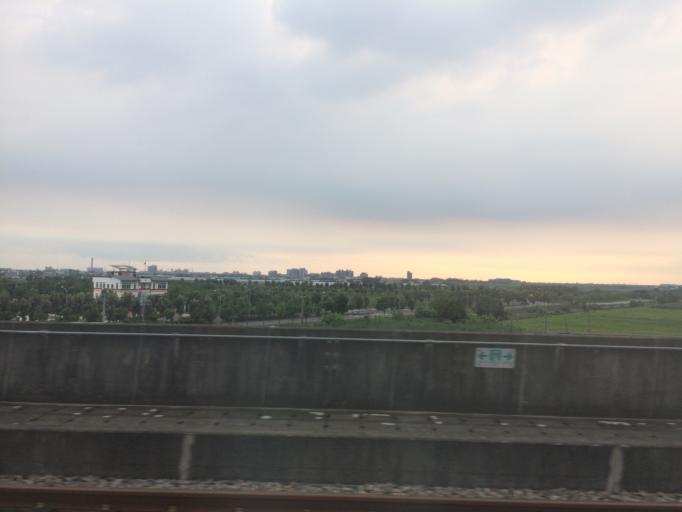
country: TW
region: Taiwan
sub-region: Chiayi
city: Taibao
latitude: 23.4642
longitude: 120.3240
